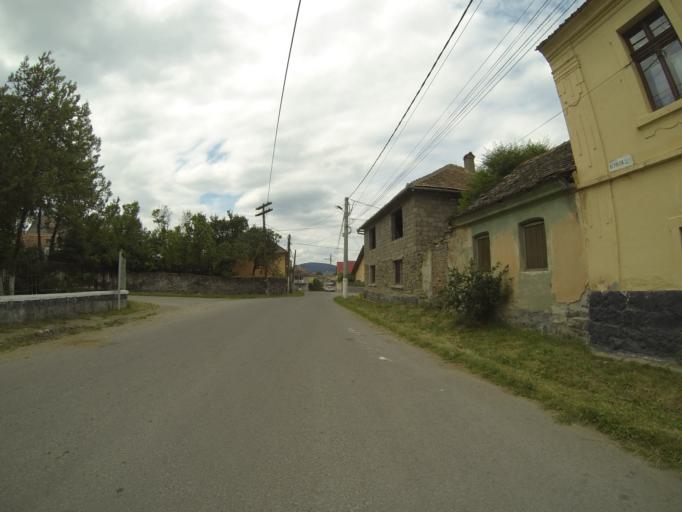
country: RO
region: Brasov
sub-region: Comuna Hoghiz
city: Hoghiz
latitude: 46.0240
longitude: 25.4080
